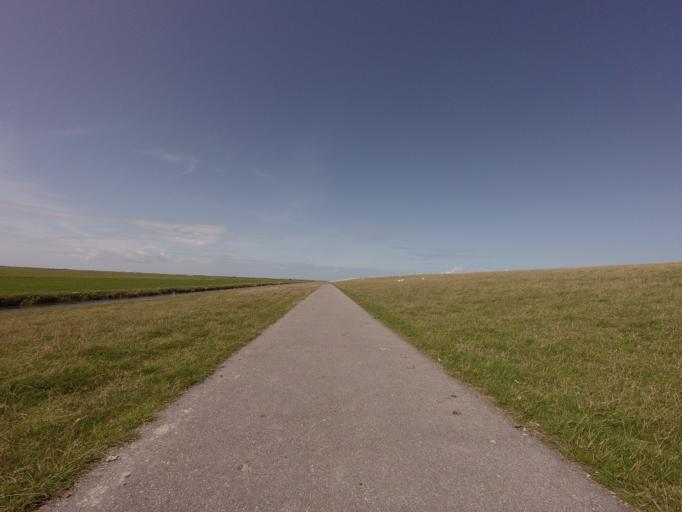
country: NL
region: Friesland
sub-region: Gemeente Dongeradeel
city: Holwerd
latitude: 53.3671
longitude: 5.8613
